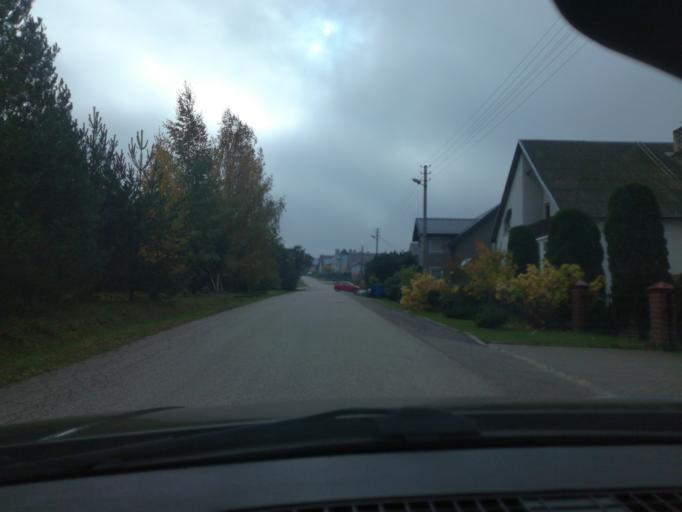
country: LT
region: Alytaus apskritis
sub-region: Alytus
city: Alytus
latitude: 54.3980
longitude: 24.0026
